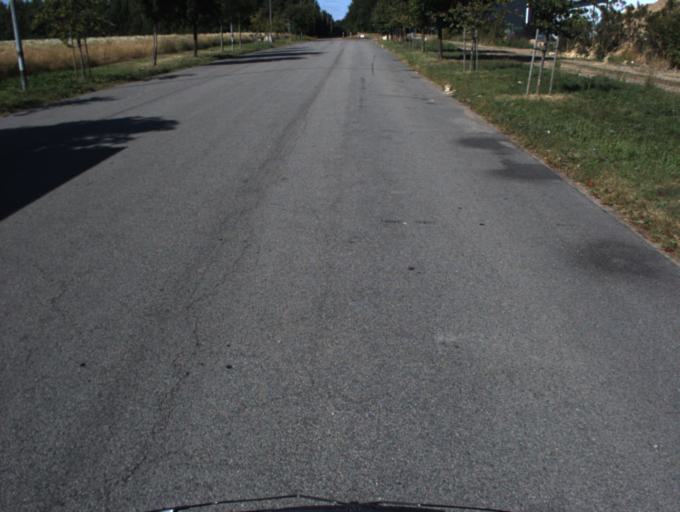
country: SE
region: Skane
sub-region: Helsingborg
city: Odakra
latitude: 56.0788
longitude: 12.7546
